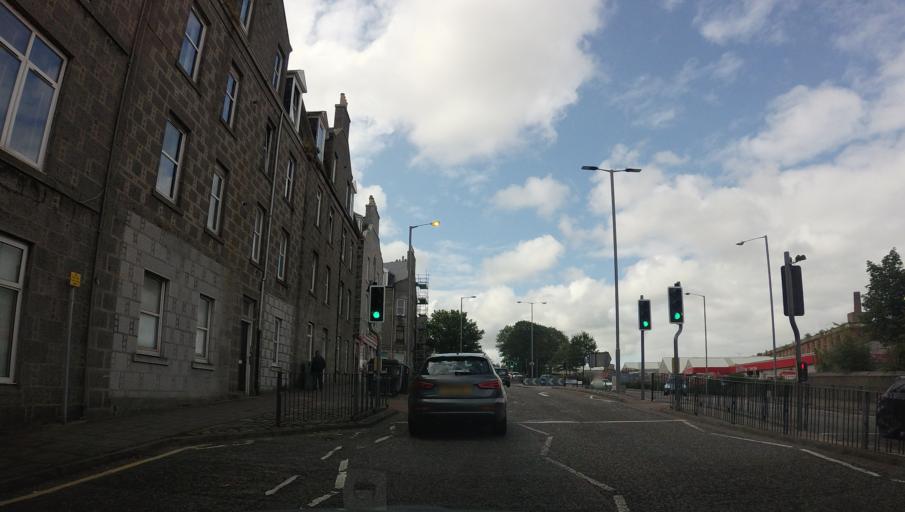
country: GB
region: Scotland
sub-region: Aberdeen City
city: Aberdeen
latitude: 57.1511
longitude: -2.1085
